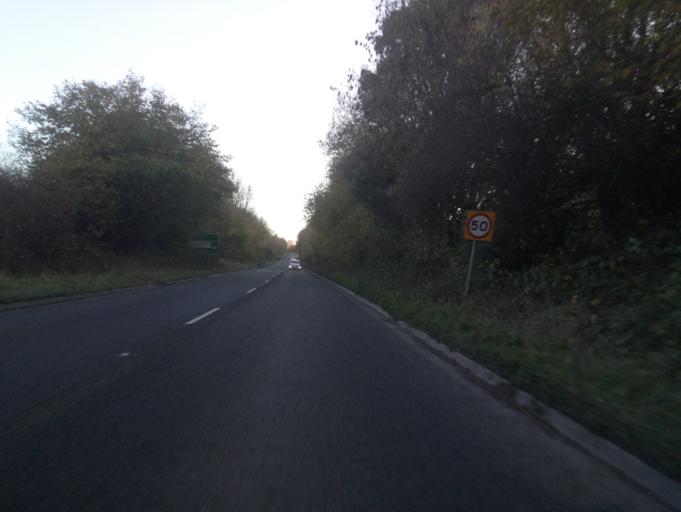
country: GB
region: England
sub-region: Wiltshire
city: Warminster
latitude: 51.1787
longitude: -2.1948
